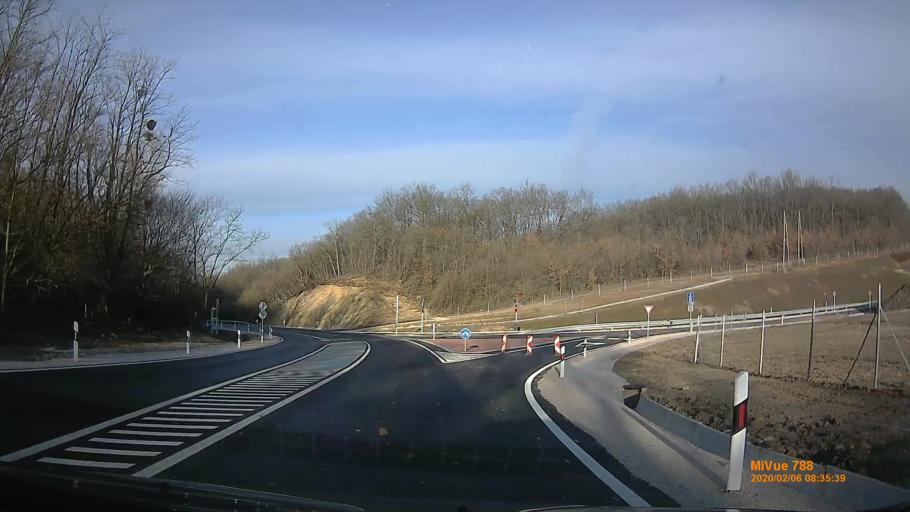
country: HU
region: Fejer
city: Szarliget
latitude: 47.5324
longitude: 18.4996
